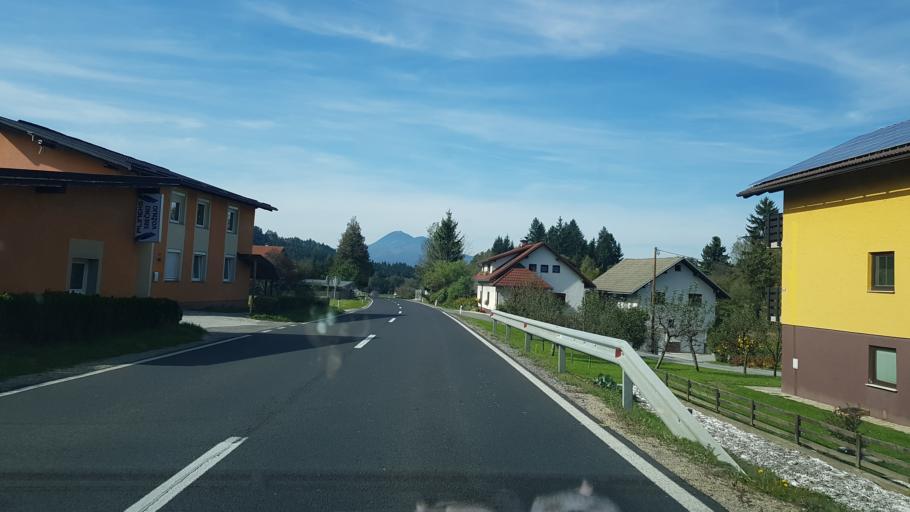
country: SI
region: Slovenj Gradec
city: Legen
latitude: 46.4477
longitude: 15.1729
